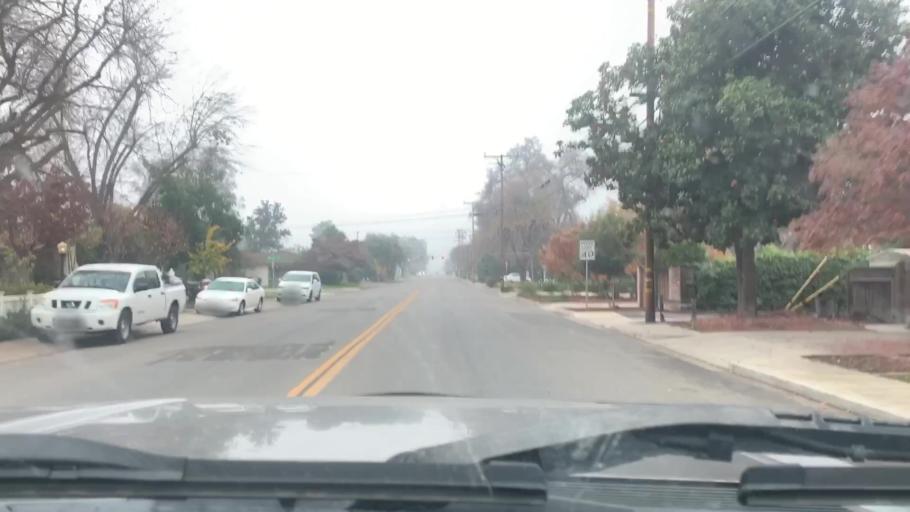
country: US
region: California
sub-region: Tulare County
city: Visalia
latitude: 36.3226
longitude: -119.3055
